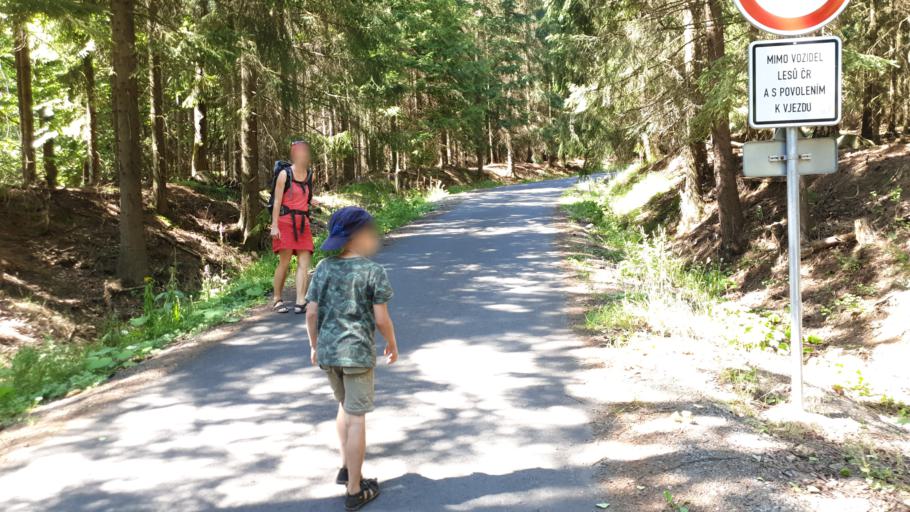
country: CZ
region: Ustecky
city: Dolni Podluzi
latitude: 50.8293
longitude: 14.5657
